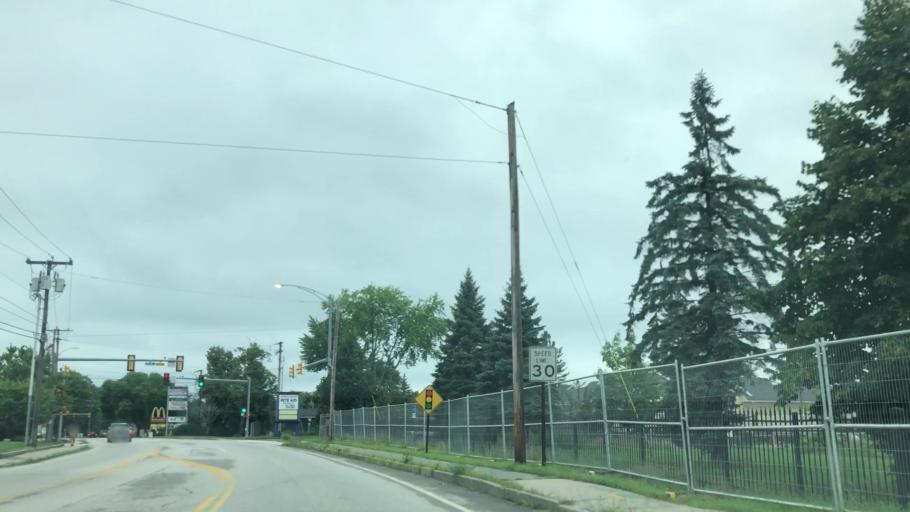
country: US
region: New Hampshire
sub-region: Hillsborough County
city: Pinardville
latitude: 42.9985
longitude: -71.5140
